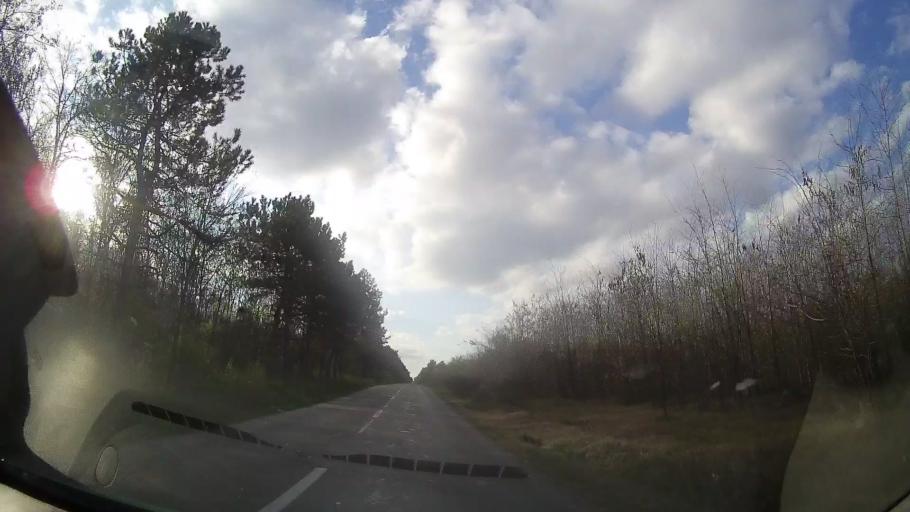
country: RO
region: Constanta
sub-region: Comuna Negru Voda
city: Negru Voda
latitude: 43.8193
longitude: 28.2665
